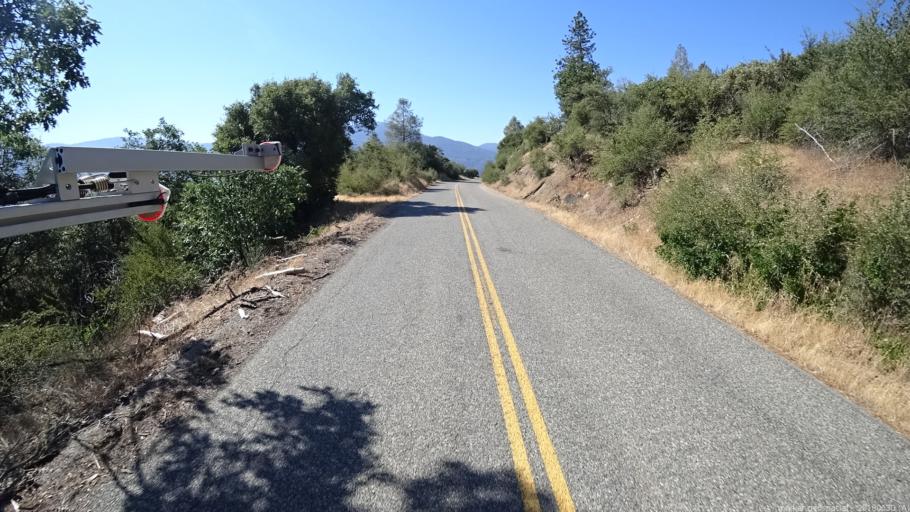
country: US
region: California
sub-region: Fresno County
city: Auberry
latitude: 37.2186
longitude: -119.3514
